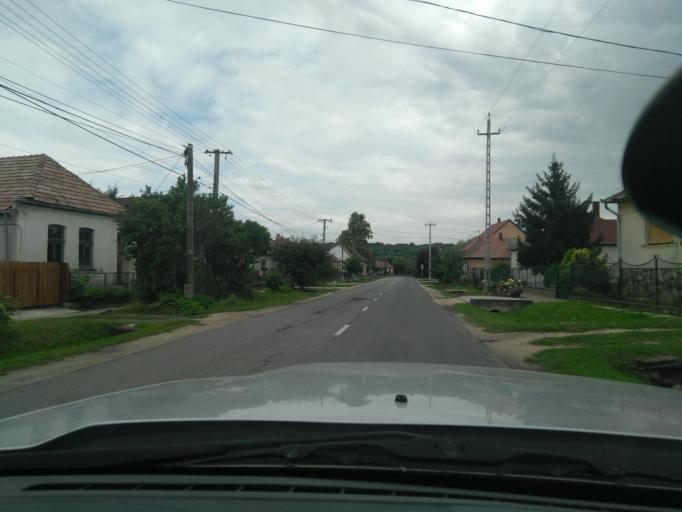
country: HU
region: Fejer
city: Val
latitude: 47.3678
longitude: 18.7409
